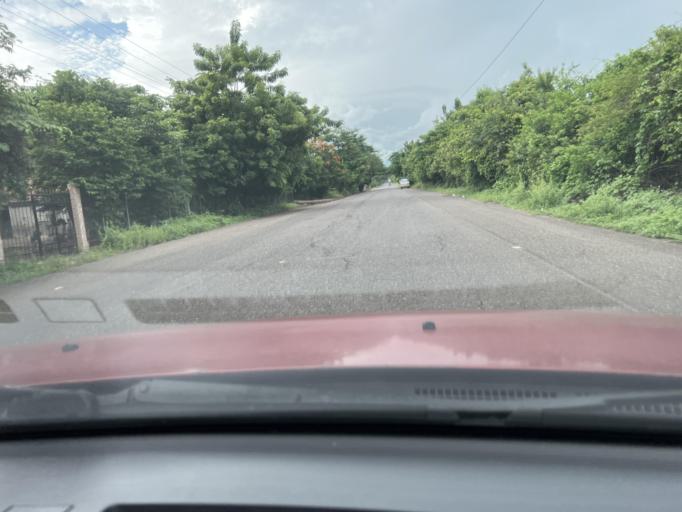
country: SV
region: La Union
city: San Alejo
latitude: 13.4161
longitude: -87.8884
